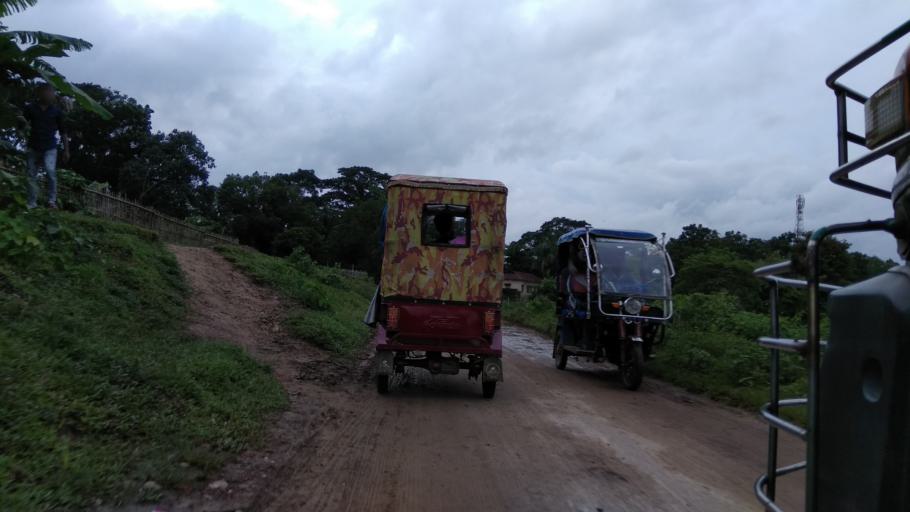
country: IN
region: Tripura
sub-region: Dhalai
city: Kamalpur
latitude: 24.2125
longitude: 91.8574
